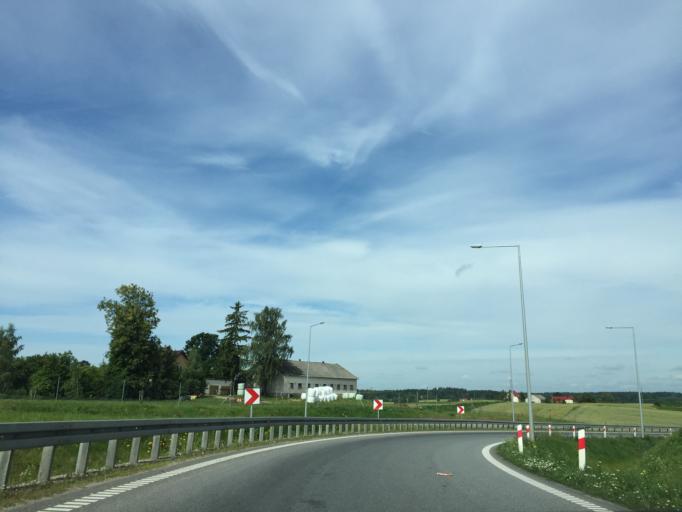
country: PL
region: Podlasie
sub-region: Powiat suwalski
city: Raczki
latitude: 53.9701
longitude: 22.7842
